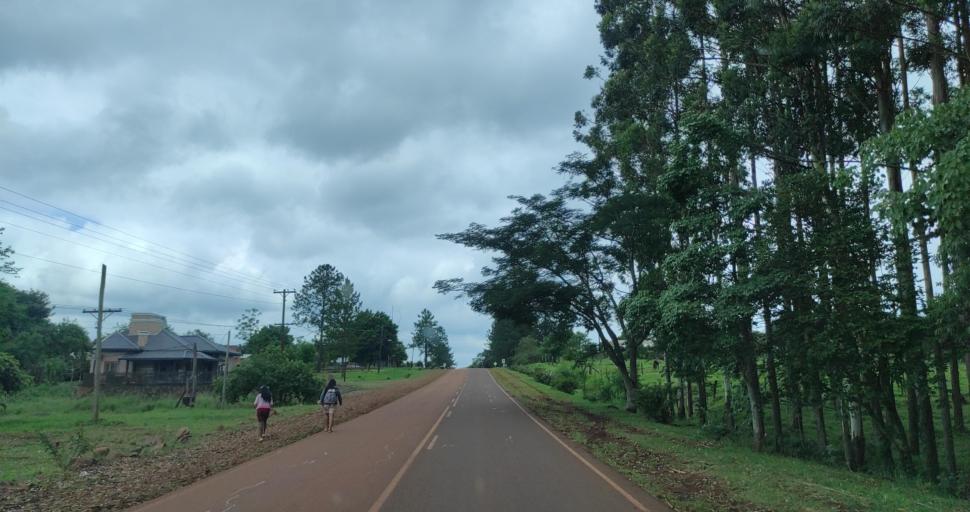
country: AR
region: Misiones
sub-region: Departamento de Veinticinco de Mayo
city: Veinticinco de Mayo
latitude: -27.3915
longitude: -54.7485
